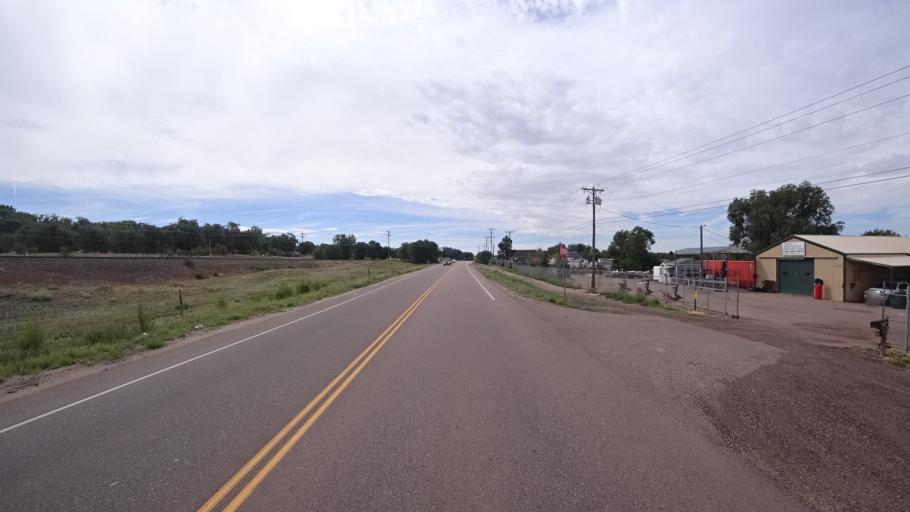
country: US
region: Colorado
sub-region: El Paso County
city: Fountain
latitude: 38.6991
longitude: -104.7068
